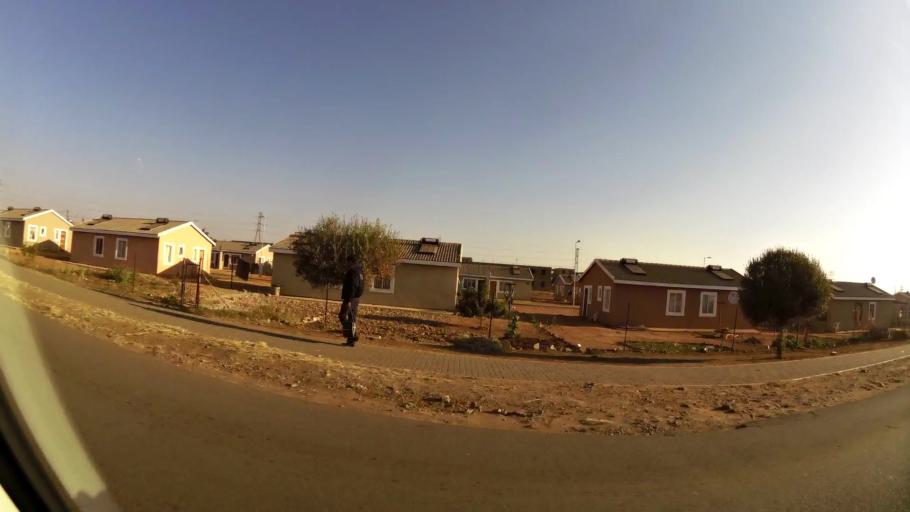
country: ZA
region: Gauteng
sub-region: City of Tshwane Metropolitan Municipality
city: Cullinan
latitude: -25.7125
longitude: 28.4040
